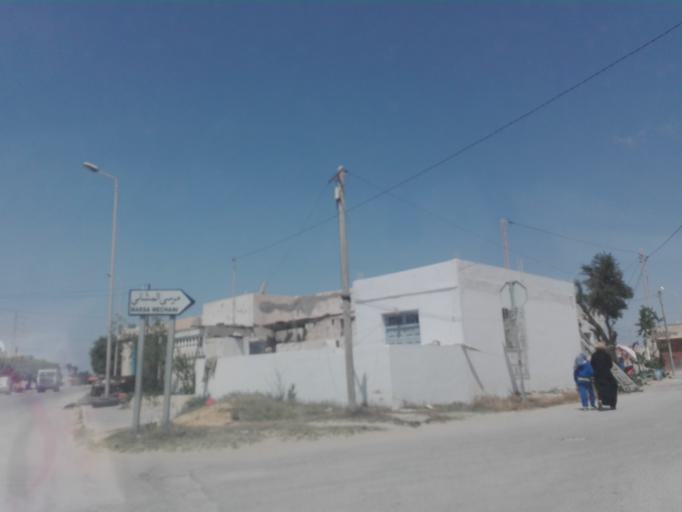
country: TN
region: Safaqis
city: Al Qarmadah
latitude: 34.6518
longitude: 11.0314
